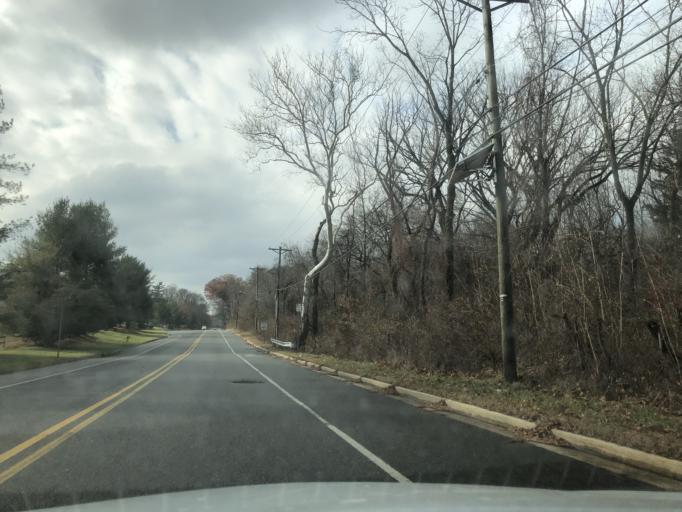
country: US
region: New Jersey
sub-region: Camden County
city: Bellmawr
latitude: 39.8470
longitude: -75.1077
